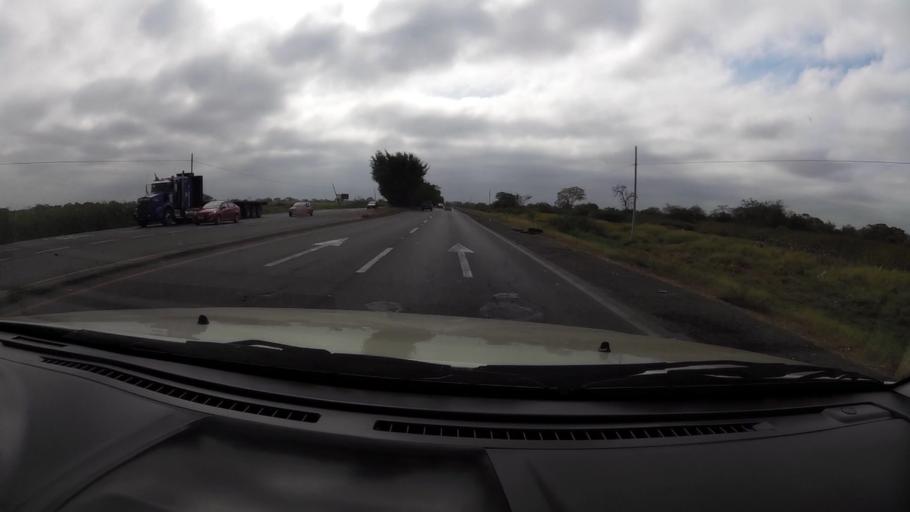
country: EC
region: Guayas
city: Eloy Alfaro
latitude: -2.2045
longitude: -79.7485
